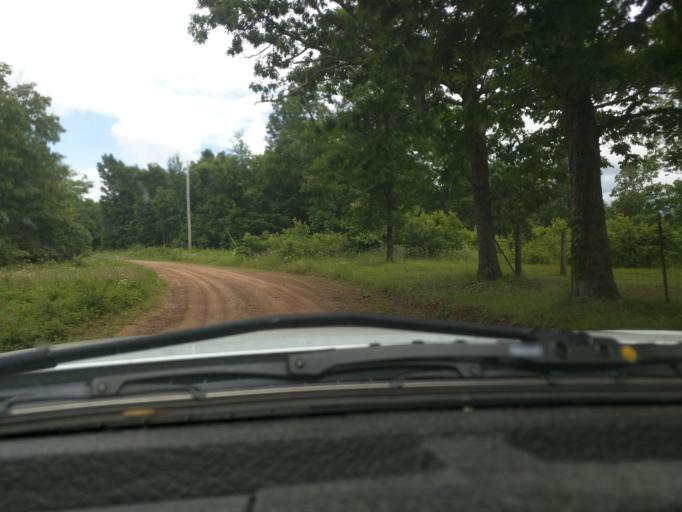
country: US
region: Arkansas
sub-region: Madison County
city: Huntsville
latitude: 35.8887
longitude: -93.5644
